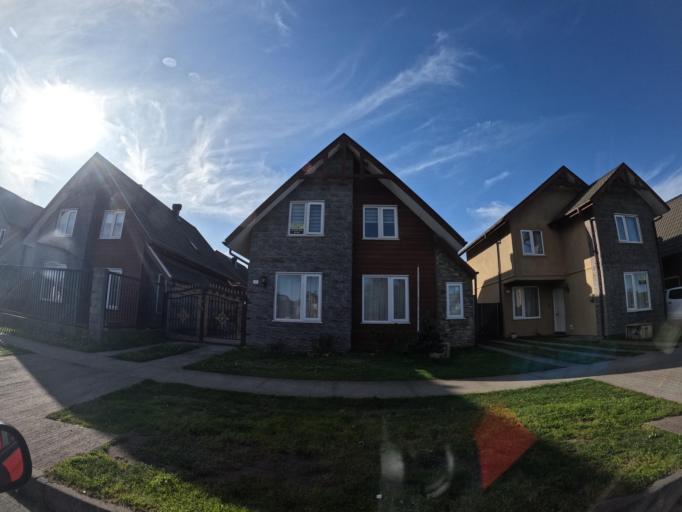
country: CL
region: Biobio
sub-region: Provincia de Concepcion
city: Concepcion
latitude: -36.7703
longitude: -73.0693
